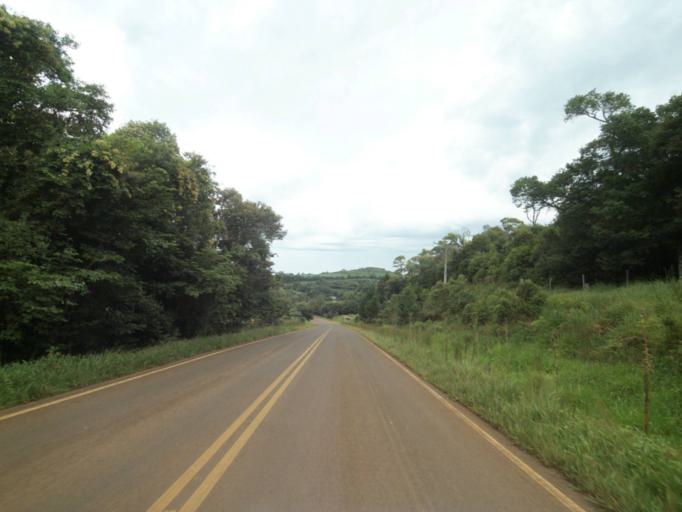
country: BR
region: Parana
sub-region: Pitanga
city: Pitanga
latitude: -24.8964
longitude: -51.9558
